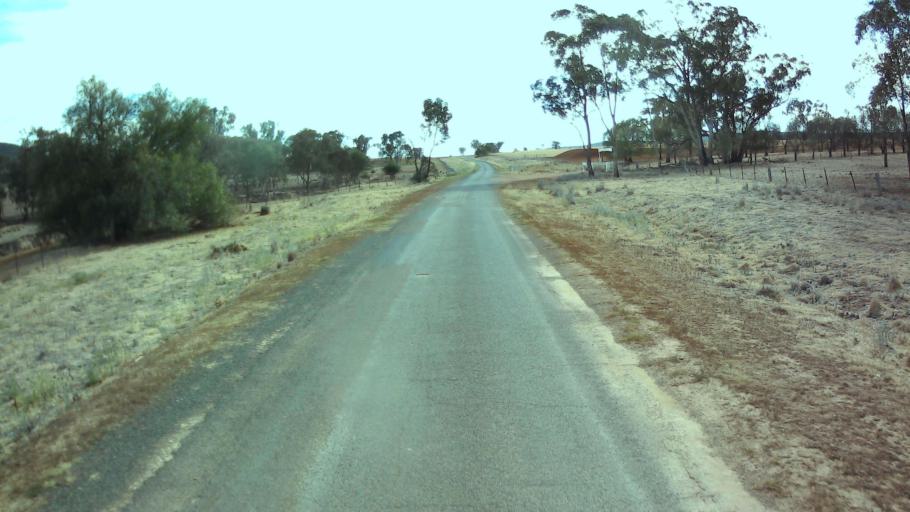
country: AU
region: New South Wales
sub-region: Weddin
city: Grenfell
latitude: -33.8394
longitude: 148.2647
